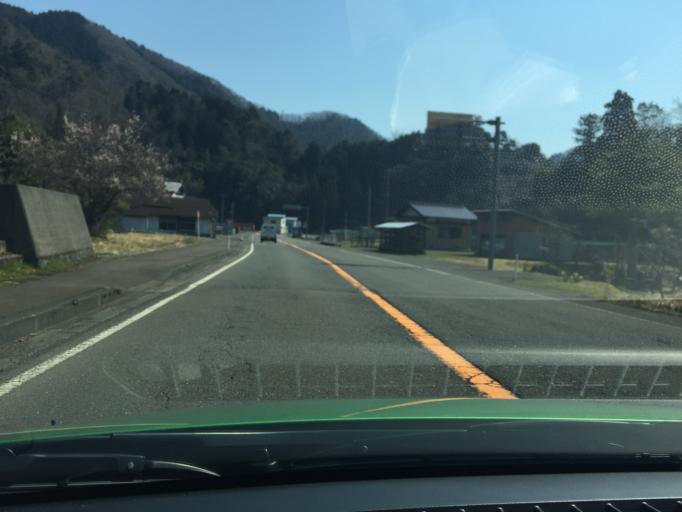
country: JP
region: Fukui
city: Obama
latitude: 35.3960
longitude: 135.5851
